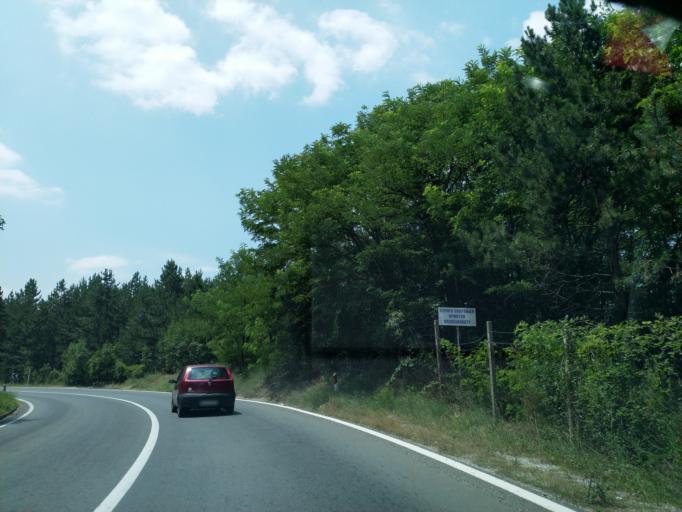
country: RS
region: Central Serbia
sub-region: Rasinski Okrug
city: Aleksandrovac
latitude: 43.4181
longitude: 21.1852
